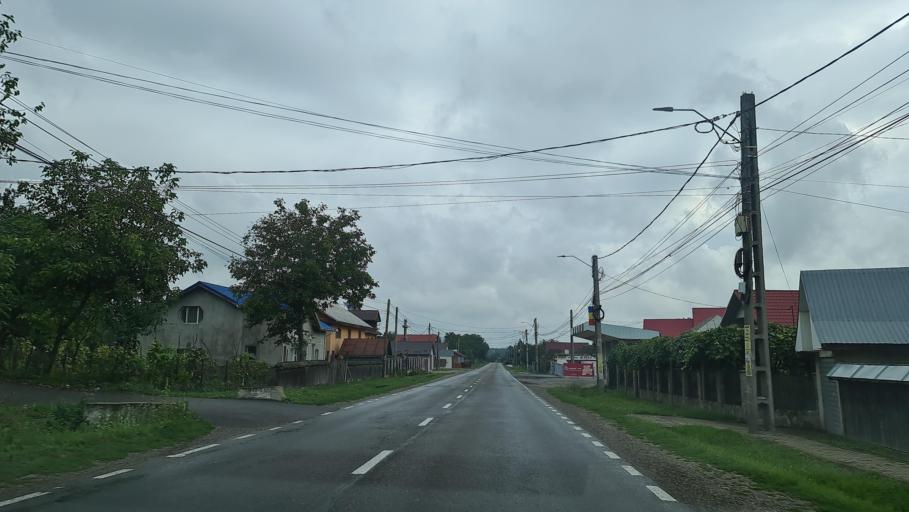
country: RO
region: Neamt
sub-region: Comuna Borlesti
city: Ruseni
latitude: 46.7821
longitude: 26.5174
